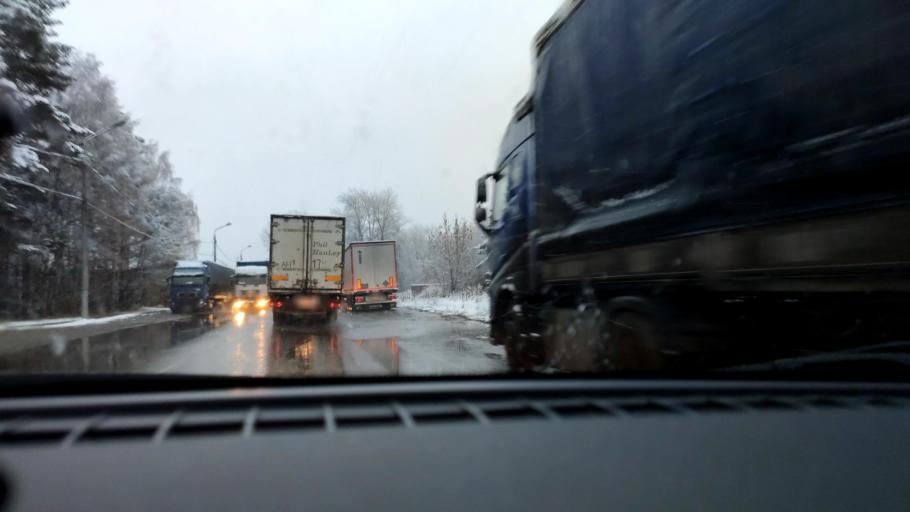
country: RU
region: Perm
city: Overyata
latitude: 58.0130
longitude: 55.9199
